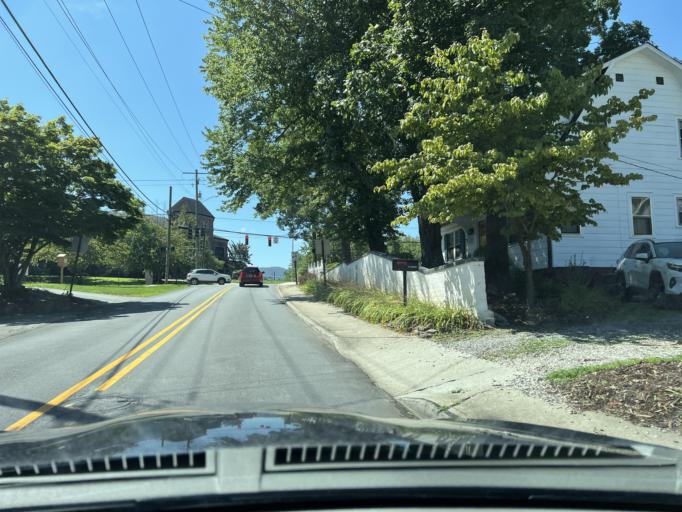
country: US
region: North Carolina
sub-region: Buncombe County
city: Biltmore Forest
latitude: 35.5651
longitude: -82.5129
